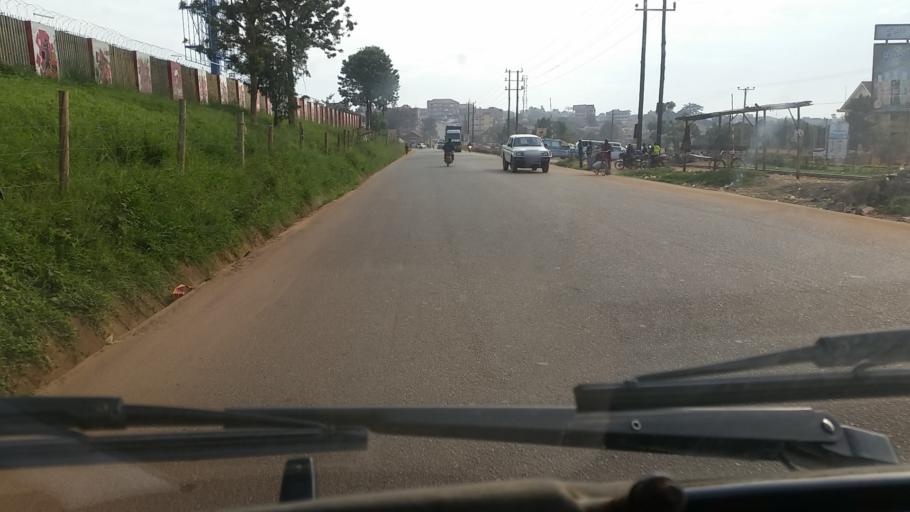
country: UG
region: Central Region
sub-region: Wakiso District
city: Bweyogerere
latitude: 0.3477
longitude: 32.6613
